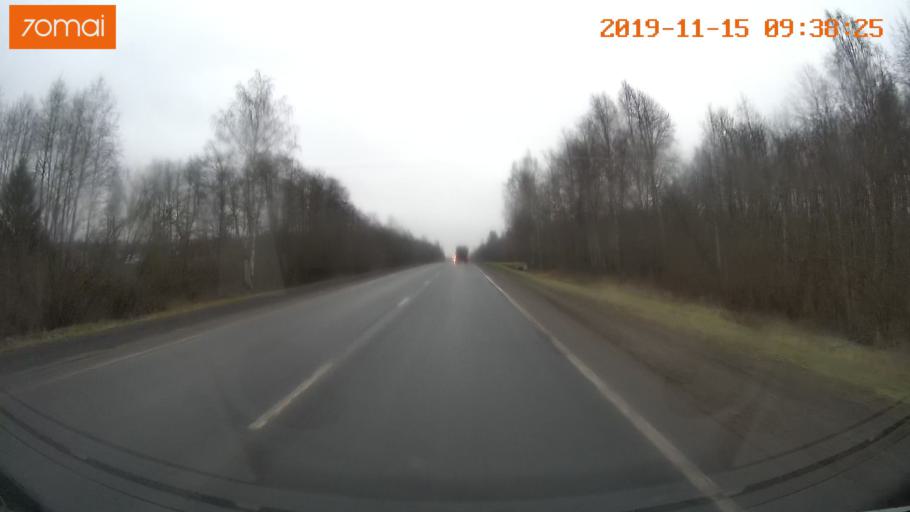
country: RU
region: Vologda
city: Sheksna
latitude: 59.2320
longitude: 38.4553
